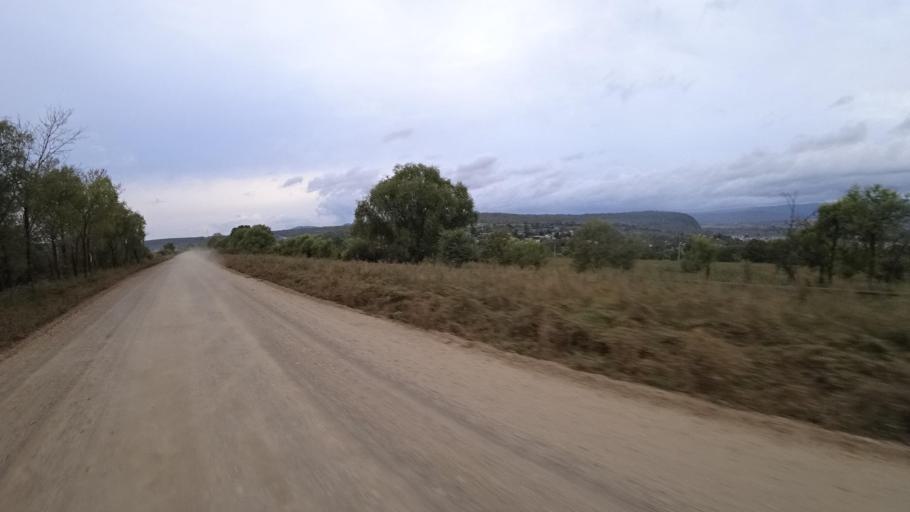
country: RU
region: Jewish Autonomous Oblast
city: Izvestkovyy
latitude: 48.9750
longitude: 131.5622
